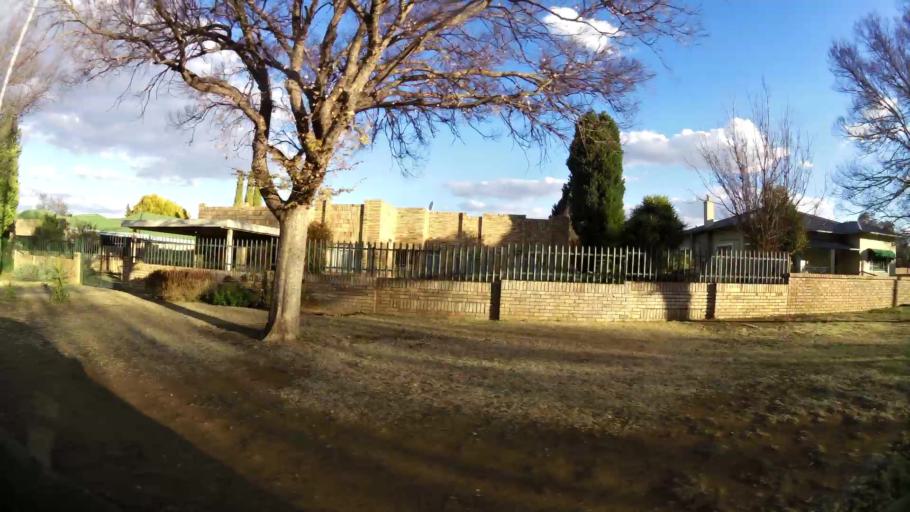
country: ZA
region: North-West
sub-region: Dr Kenneth Kaunda District Municipality
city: Potchefstroom
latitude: -26.7310
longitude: 27.0961
